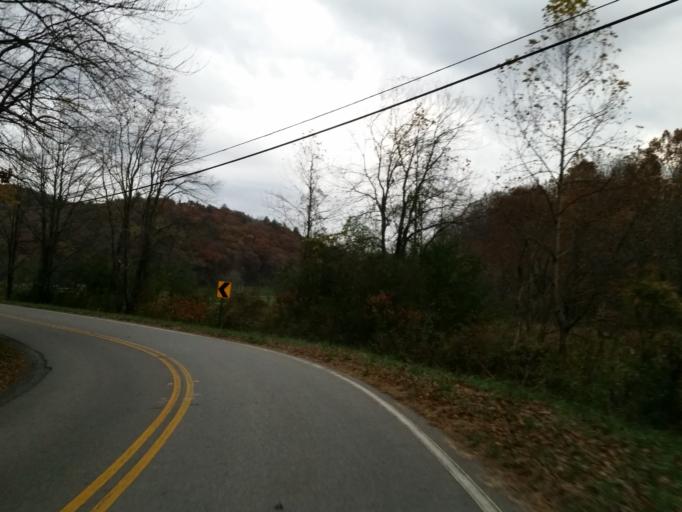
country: US
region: Georgia
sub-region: Union County
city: Blairsville
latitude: 34.7169
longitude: -84.0667
